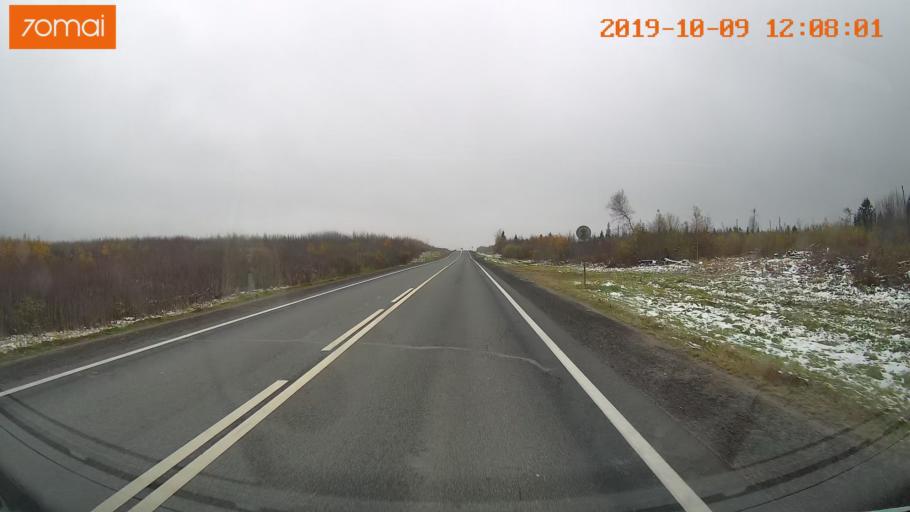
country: RU
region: Jaroslavl
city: Prechistoye
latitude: 58.5921
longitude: 40.3455
